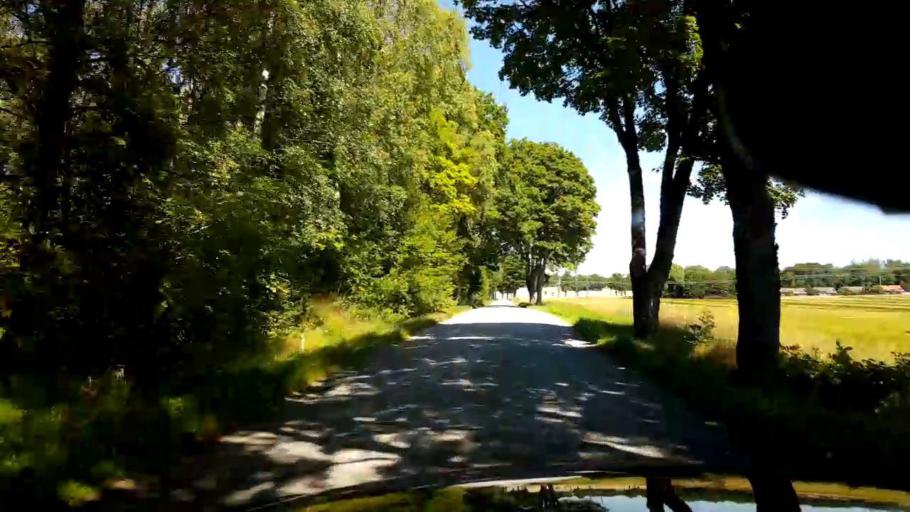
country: SE
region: Stockholm
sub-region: Upplands-Bro Kommun
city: Bro
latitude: 59.5958
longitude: 17.6422
